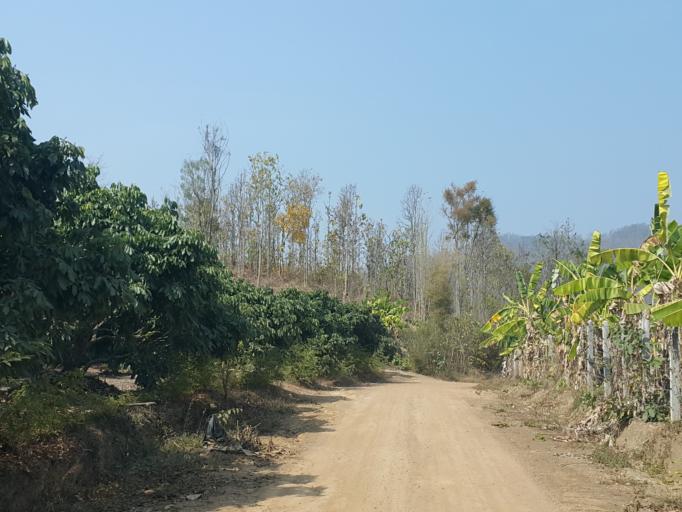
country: TH
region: Chiang Mai
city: Hang Dong
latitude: 18.7303
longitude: 98.8595
